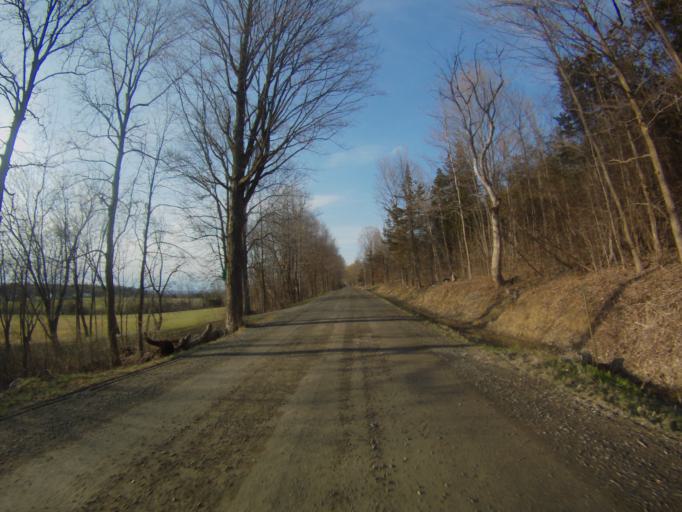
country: US
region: Vermont
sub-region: Addison County
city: Vergennes
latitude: 44.0552
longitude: -73.2922
